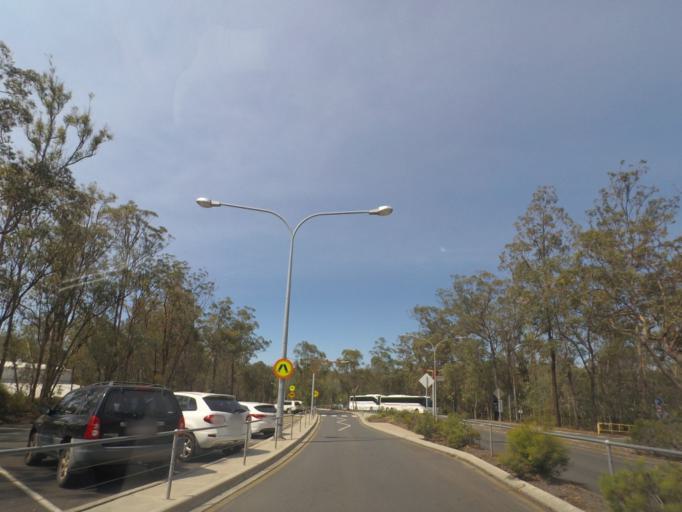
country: AU
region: Queensland
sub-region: Brisbane
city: Nathan
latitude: -27.5533
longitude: 153.0566
